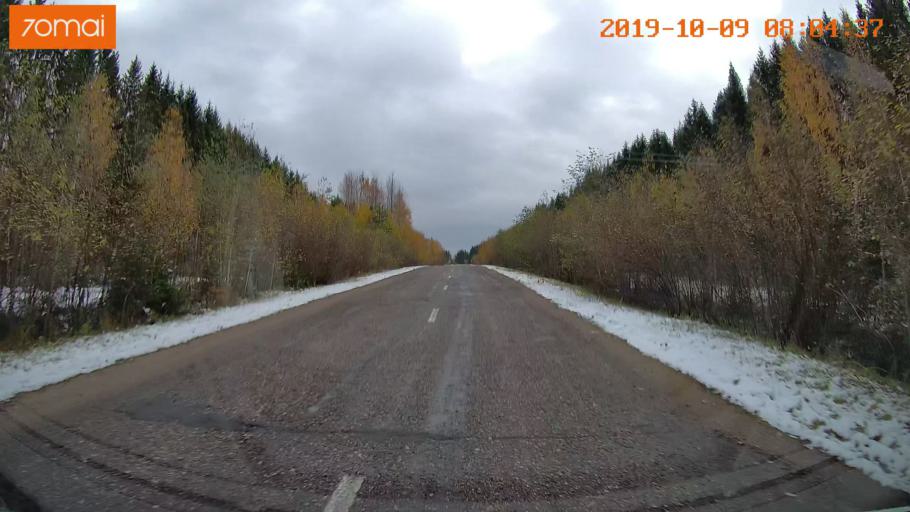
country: RU
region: Jaroslavl
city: Kukoboy
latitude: 58.6914
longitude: 40.0298
